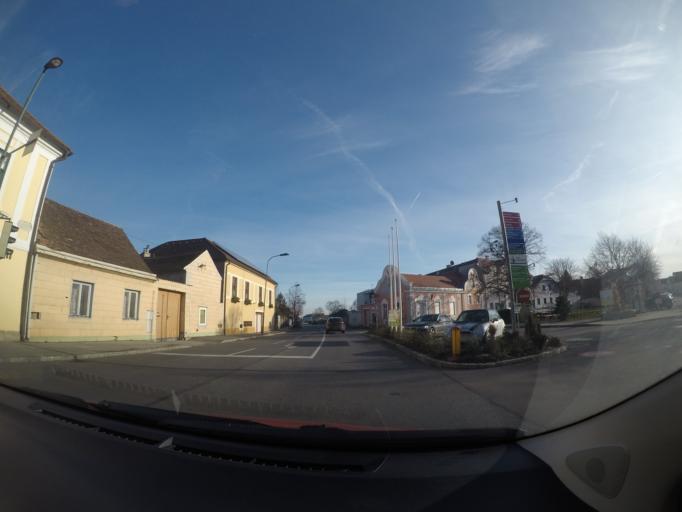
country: AT
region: Lower Austria
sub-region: Politischer Bezirk Baden
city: Pfaffstatten
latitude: 48.0172
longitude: 16.2663
